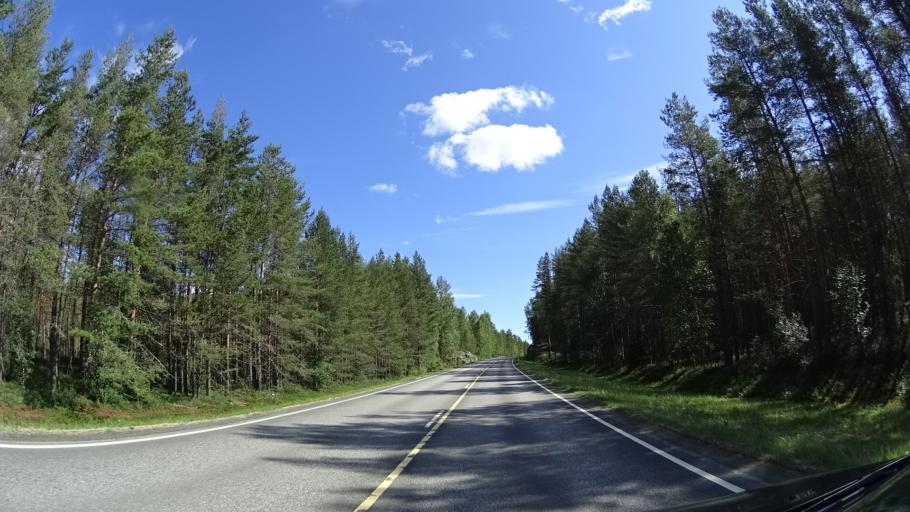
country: FI
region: Pirkanmaa
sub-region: Luoteis-Pirkanmaa
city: Kihnioe
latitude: 62.2170
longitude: 23.2608
